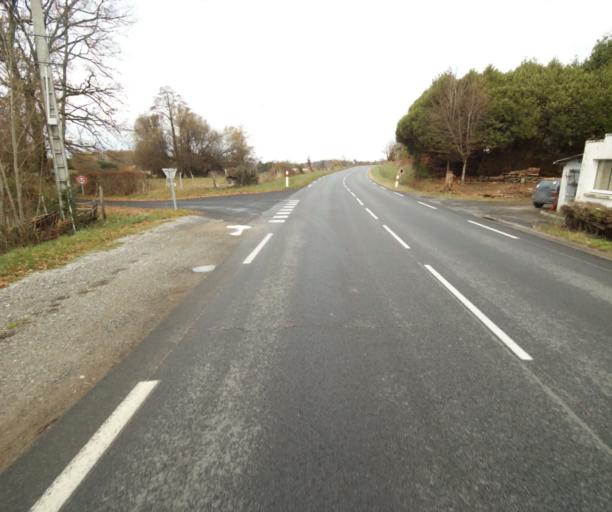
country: FR
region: Limousin
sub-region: Departement de la Correze
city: Saint-Mexant
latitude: 45.2680
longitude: 1.6366
